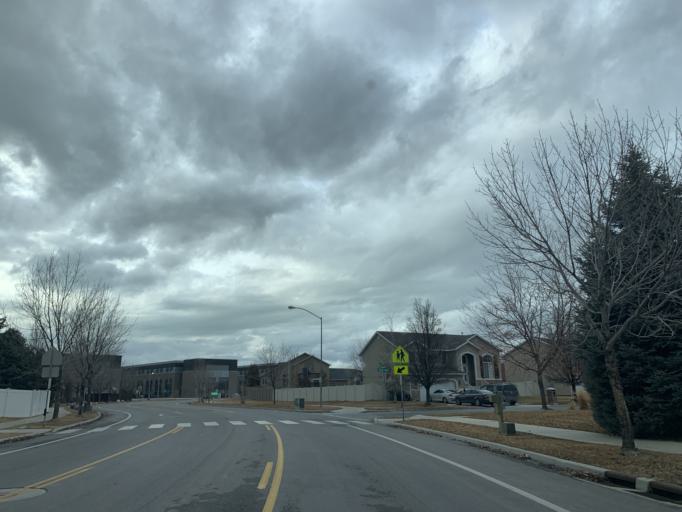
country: US
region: Utah
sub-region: Utah County
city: Orem
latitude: 40.2486
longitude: -111.7121
